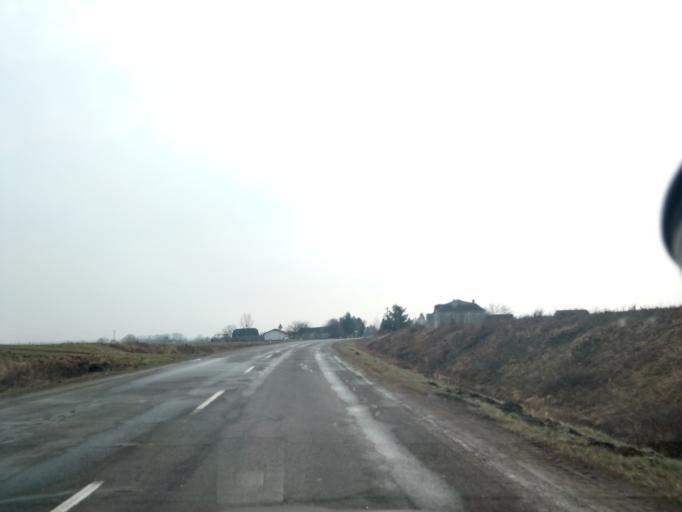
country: SK
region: Kosicky
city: Secovce
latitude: 48.6187
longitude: 21.5961
